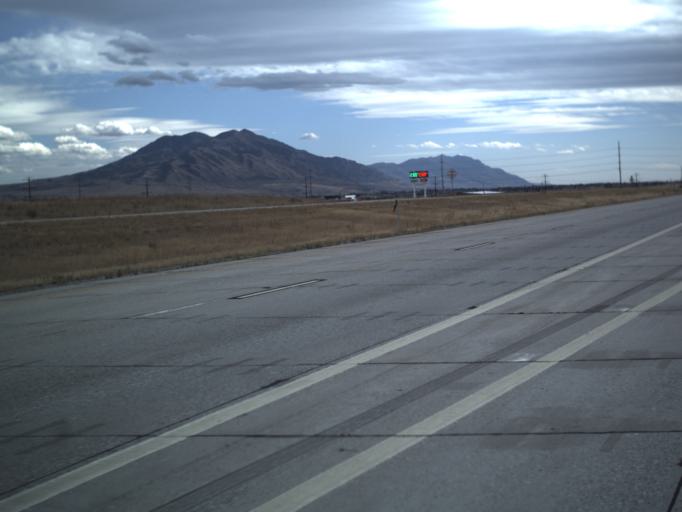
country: US
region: Utah
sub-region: Box Elder County
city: Garland
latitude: 41.8916
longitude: -112.1708
